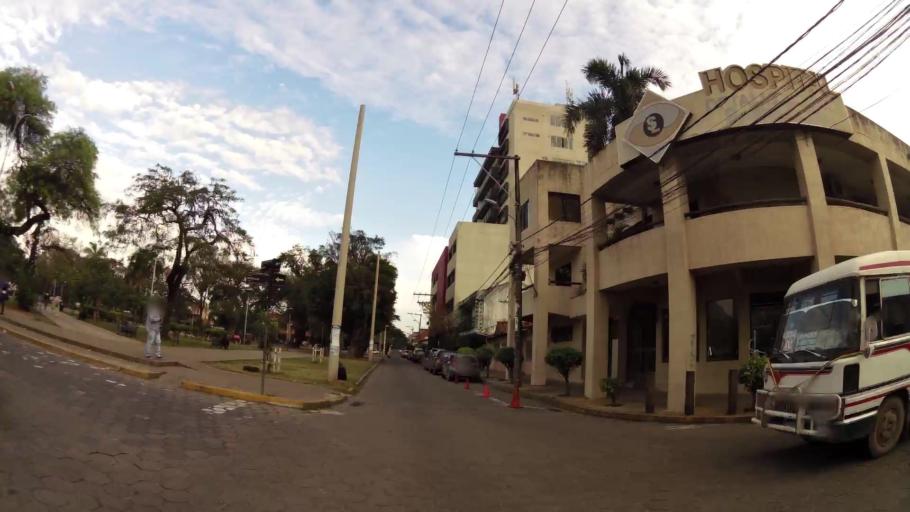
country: BO
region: Santa Cruz
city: Santa Cruz de la Sierra
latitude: -17.7810
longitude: -63.1738
